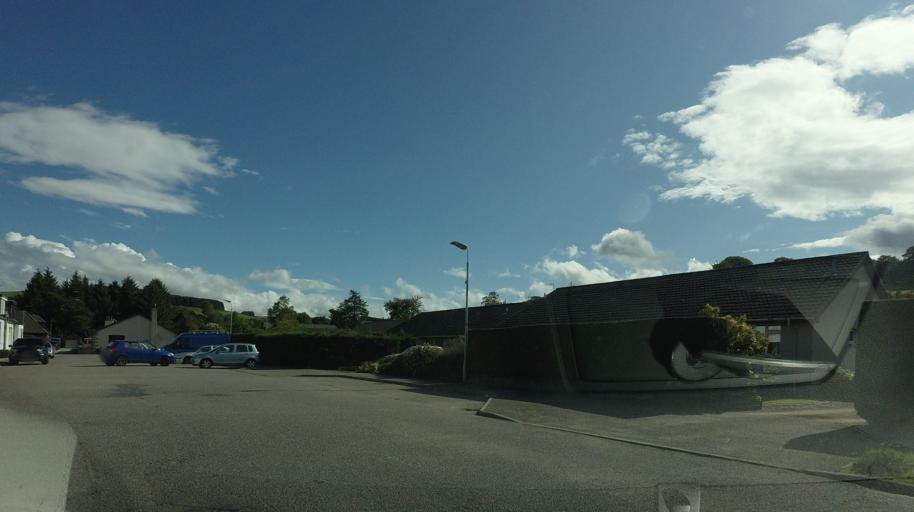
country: GB
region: Scotland
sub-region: Aberdeenshire
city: Torphins
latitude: 57.1277
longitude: -2.6882
